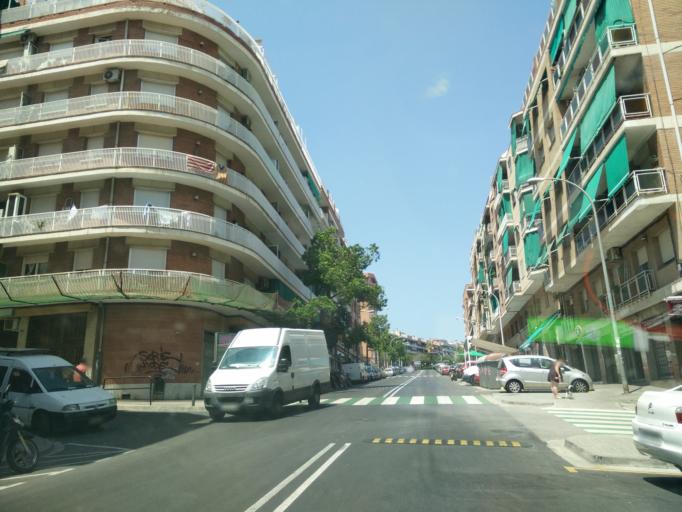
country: ES
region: Catalonia
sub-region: Provincia de Barcelona
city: Badalona
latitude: 41.4527
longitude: 2.2377
